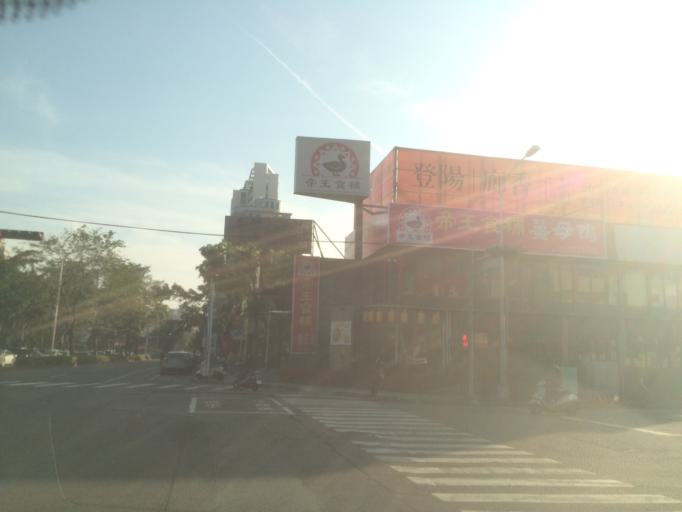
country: TW
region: Taiwan
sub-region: Taichung City
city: Taichung
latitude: 24.1884
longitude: 120.6862
